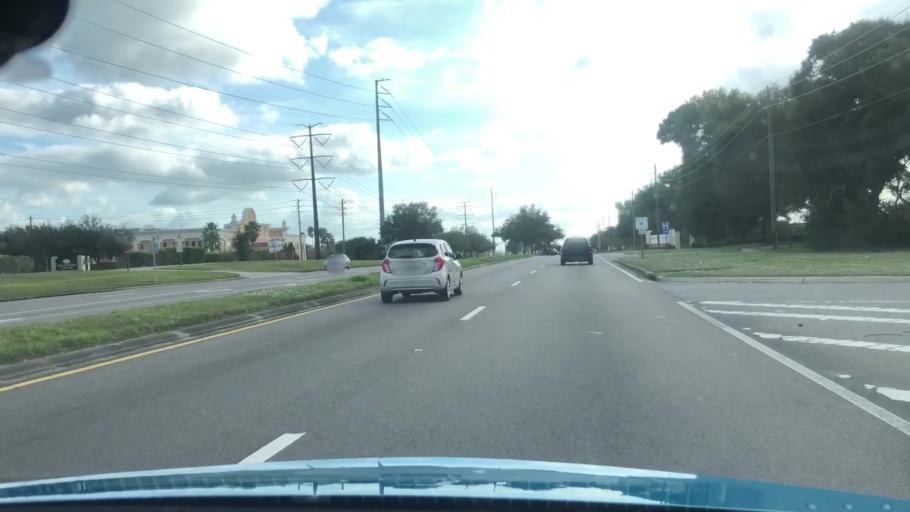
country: US
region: Florida
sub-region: Seminole County
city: Heathrow
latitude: 28.7855
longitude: -81.3473
